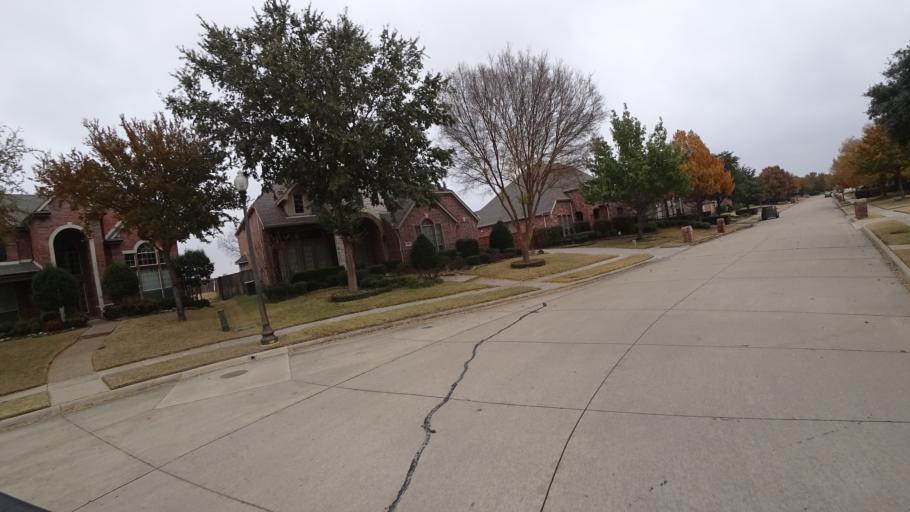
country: US
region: Texas
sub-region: Denton County
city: Lewisville
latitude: 33.0383
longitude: -96.9322
